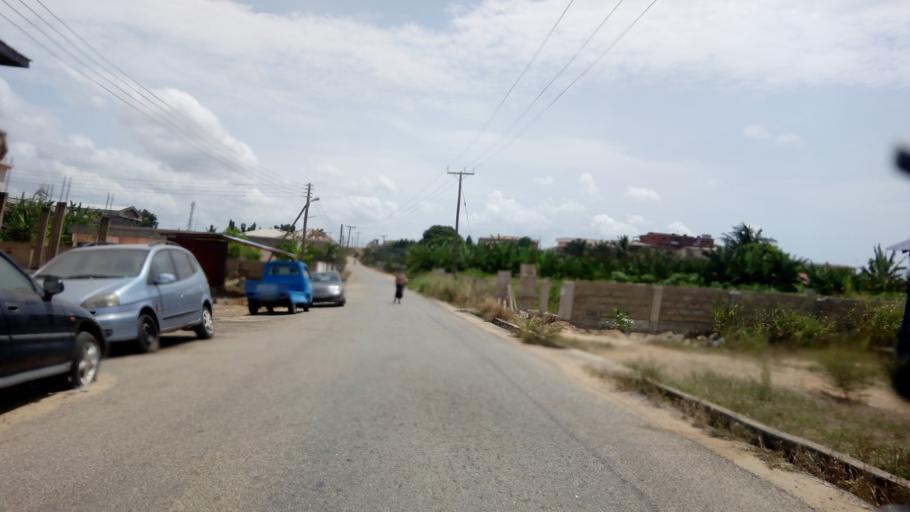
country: GH
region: Central
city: Cape Coast
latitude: 5.1240
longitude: -1.2758
